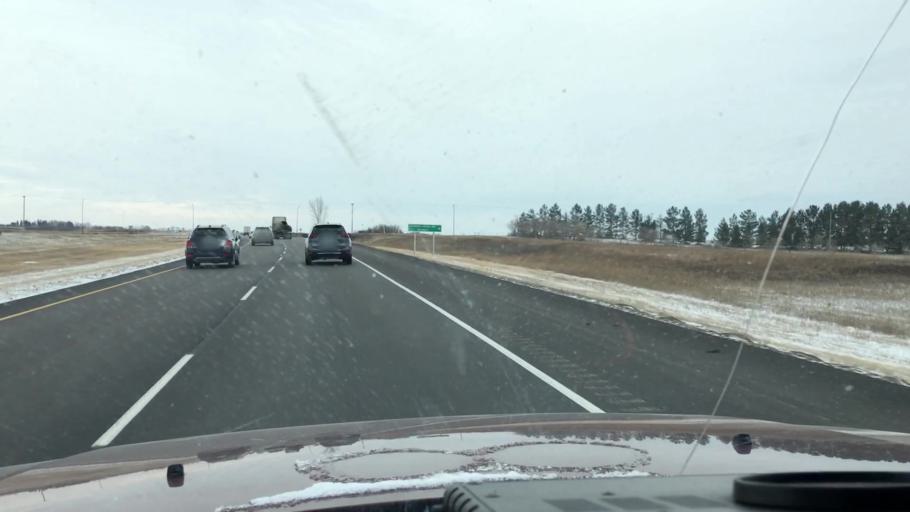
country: CA
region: Saskatchewan
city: Saskatoon
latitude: 51.8553
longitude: -106.5082
